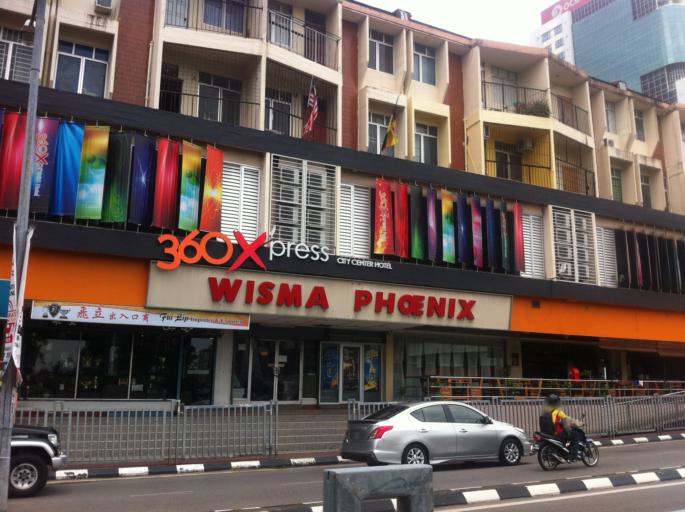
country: MY
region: Sarawak
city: Kuching
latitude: 1.5544
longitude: 110.3530
